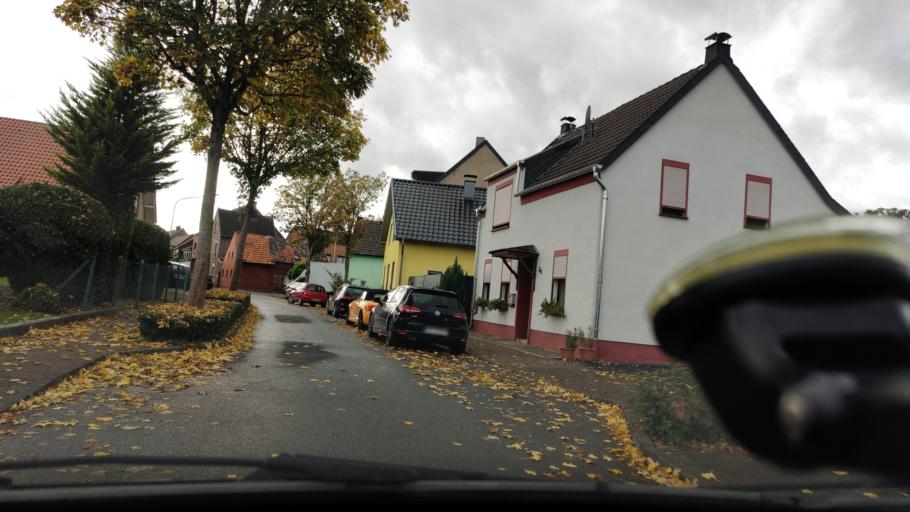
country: DE
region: North Rhine-Westphalia
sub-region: Regierungsbezirk Koln
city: Heinsberg
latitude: 51.0674
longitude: 6.0817
